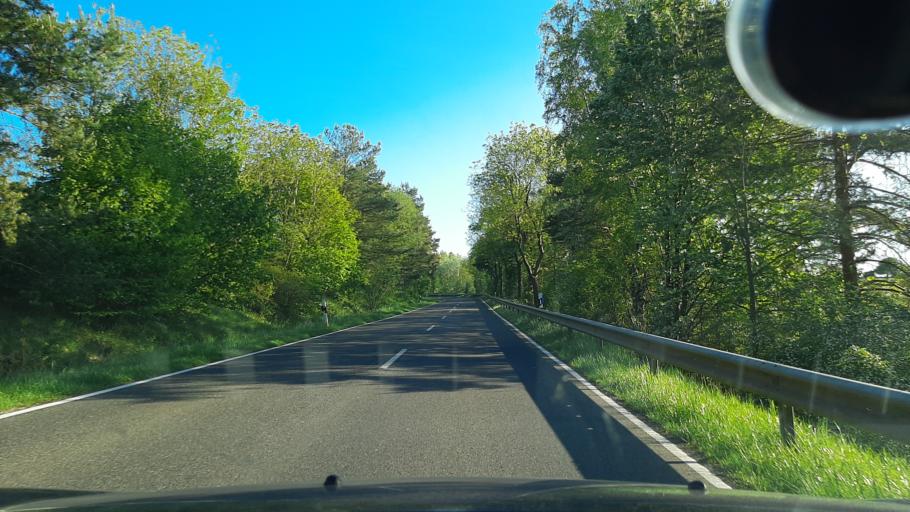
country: DE
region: North Rhine-Westphalia
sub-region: Regierungsbezirk Koln
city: Nettersheim
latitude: 50.5289
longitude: 6.6568
